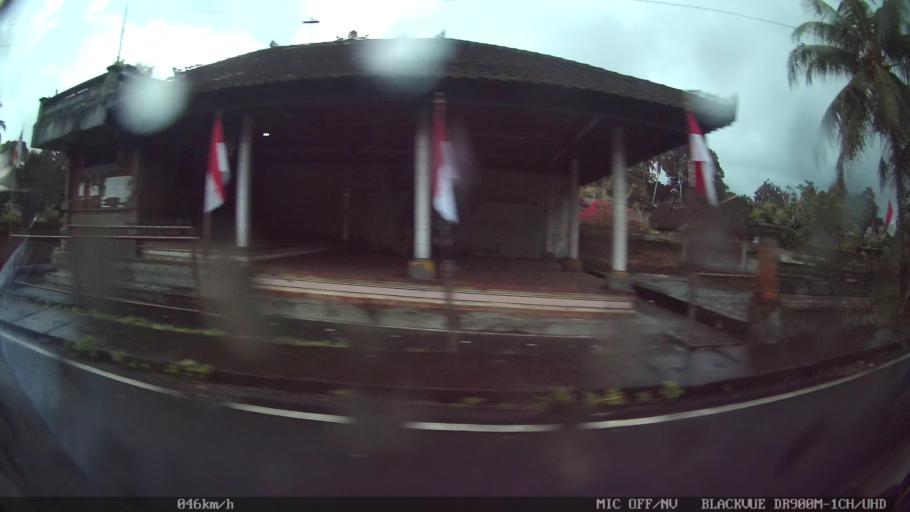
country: ID
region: Bali
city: Banjar Sayanbaleran
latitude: -8.5066
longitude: 115.1875
